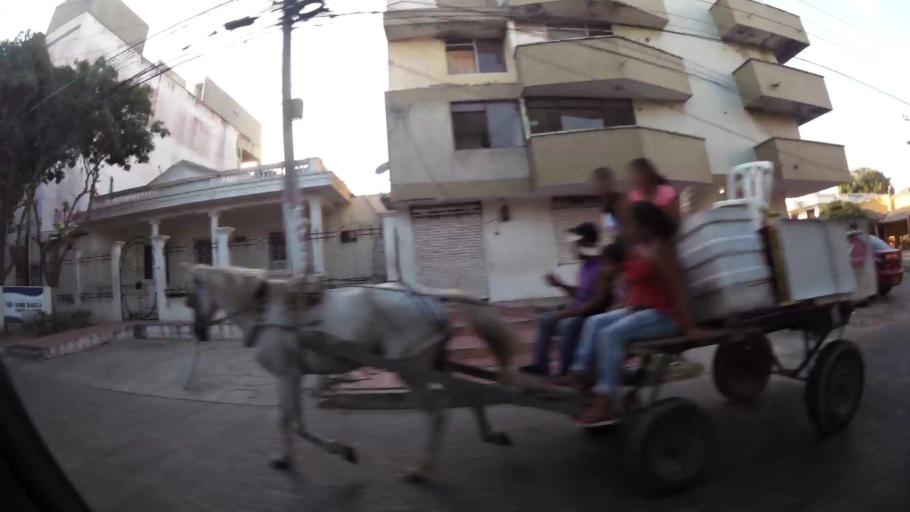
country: CO
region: Atlantico
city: Barranquilla
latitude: 10.9821
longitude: -74.7911
